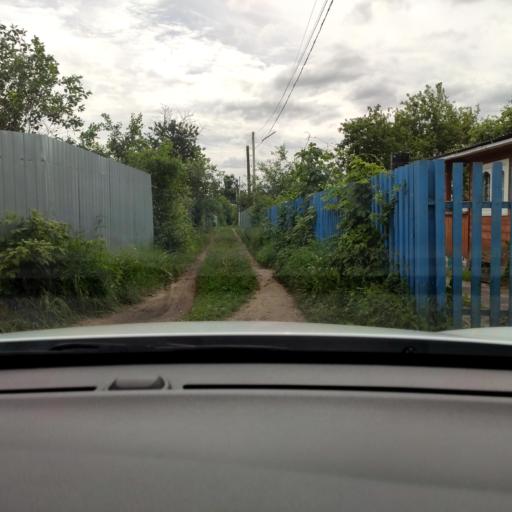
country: RU
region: Tatarstan
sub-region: Gorod Kazan'
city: Kazan
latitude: 55.8712
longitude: 49.1046
